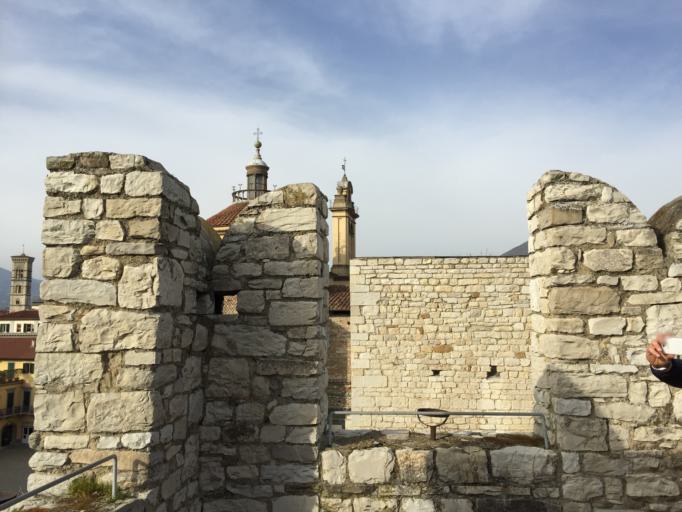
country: IT
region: Tuscany
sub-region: Provincia di Prato
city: Prato
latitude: 43.8789
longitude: 11.0982
